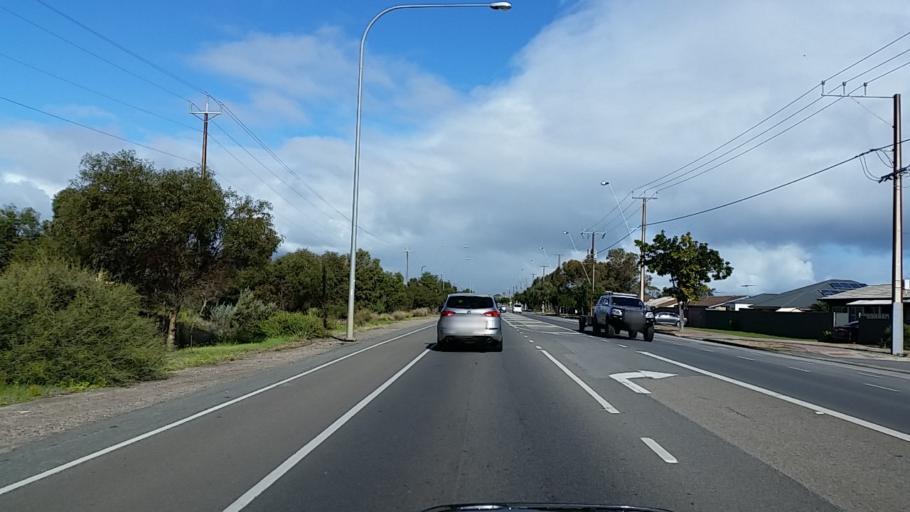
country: AU
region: South Australia
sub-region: Onkaparinga
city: Seaford
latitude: -35.1741
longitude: 138.4762
